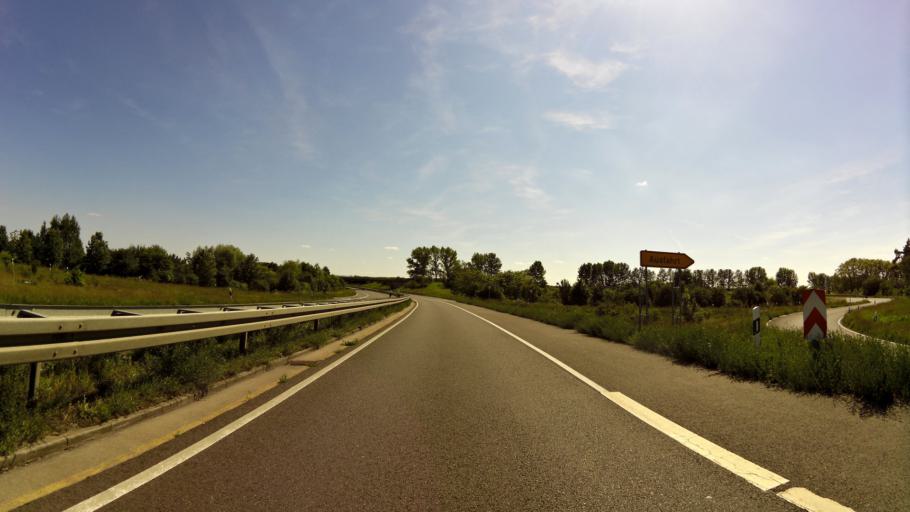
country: DE
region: Brandenburg
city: Frankfurt (Oder)
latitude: 52.3298
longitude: 14.4750
